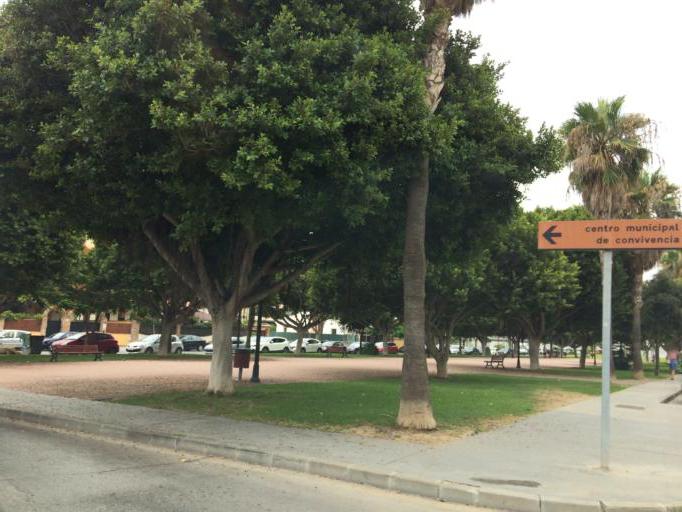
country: ES
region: Andalusia
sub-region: Provincia de Malaga
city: Torremolinos
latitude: 36.6344
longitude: -4.4913
